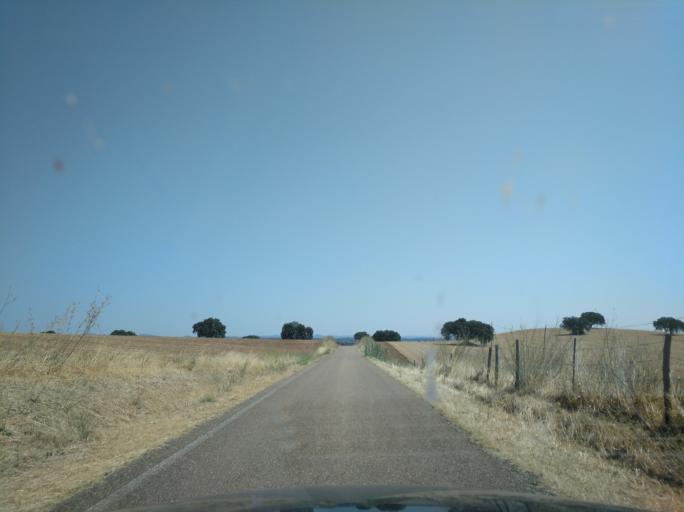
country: PT
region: Portalegre
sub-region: Campo Maior
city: Campo Maior
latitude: 39.0311
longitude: -7.0024
